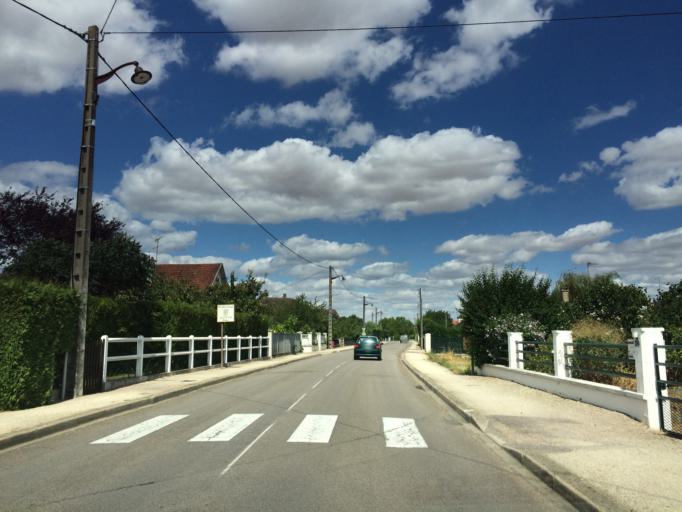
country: FR
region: Bourgogne
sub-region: Departement de l'Yonne
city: Laroche-Saint-Cydroine
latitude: 47.9475
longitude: 3.4954
